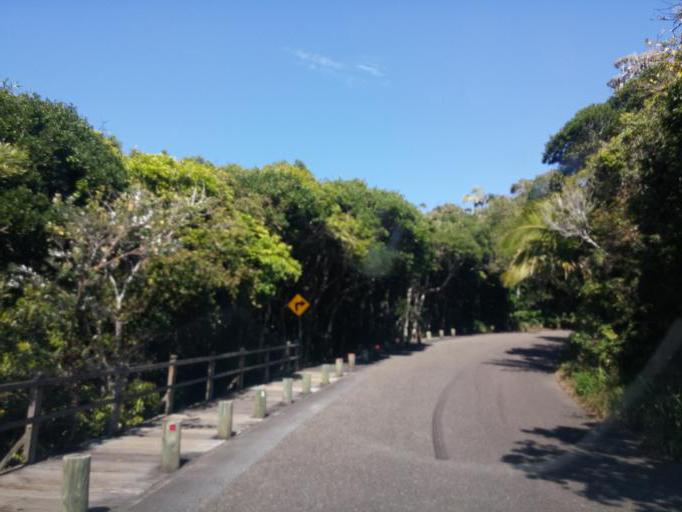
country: AU
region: New South Wales
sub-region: Port Macquarie-Hastings
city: Port Macquarie
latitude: -31.4598
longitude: 152.9320
